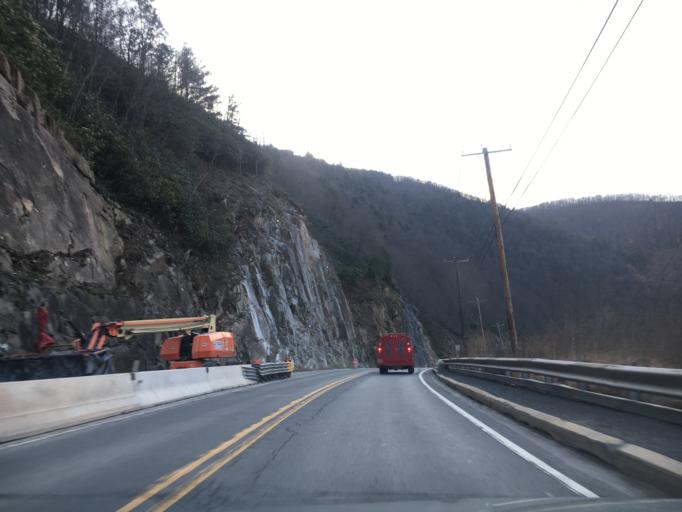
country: US
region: Pennsylvania
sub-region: Carbon County
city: Jim Thorpe
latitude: 40.8594
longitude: -75.7305
